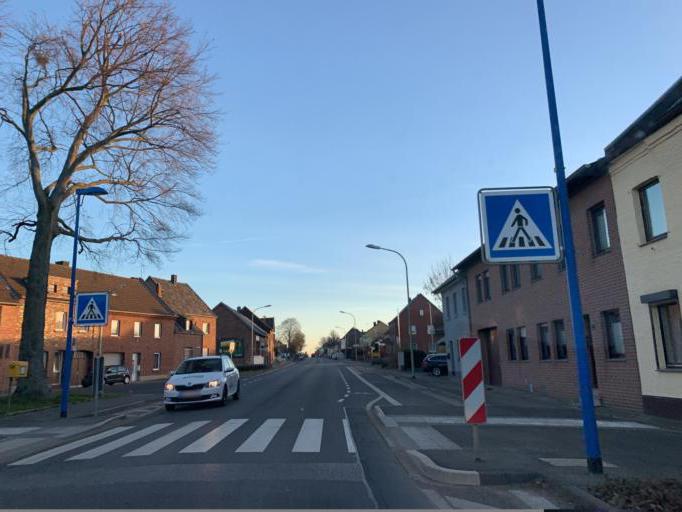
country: DE
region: North Rhine-Westphalia
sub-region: Regierungsbezirk Koln
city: Titz
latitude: 51.0066
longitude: 6.4281
